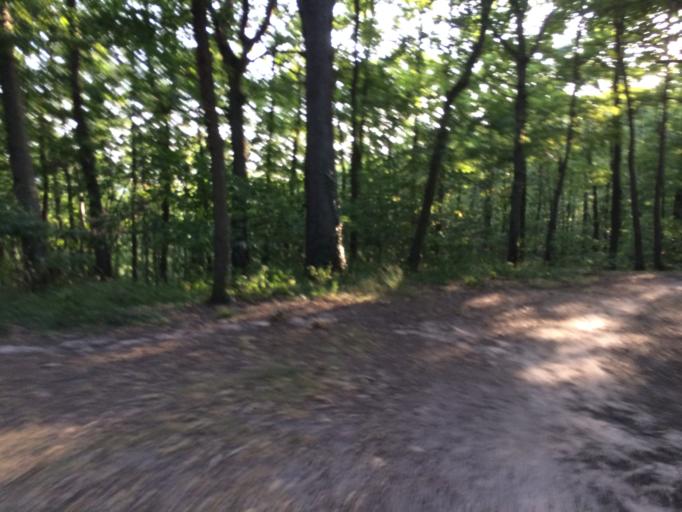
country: FR
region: Ile-de-France
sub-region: Departement de l'Essonne
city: Igny
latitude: 48.7431
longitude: 2.2461
